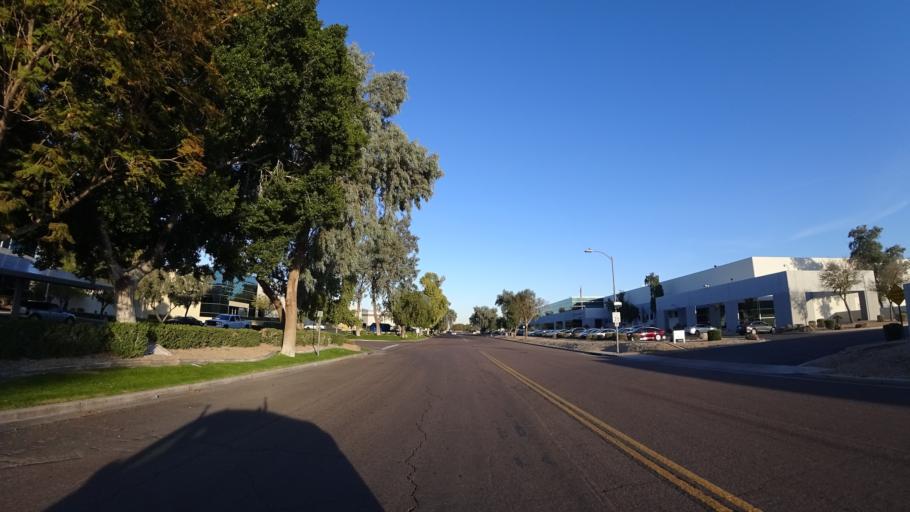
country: US
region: Arizona
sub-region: Maricopa County
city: Phoenix
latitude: 33.4232
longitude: -112.0605
